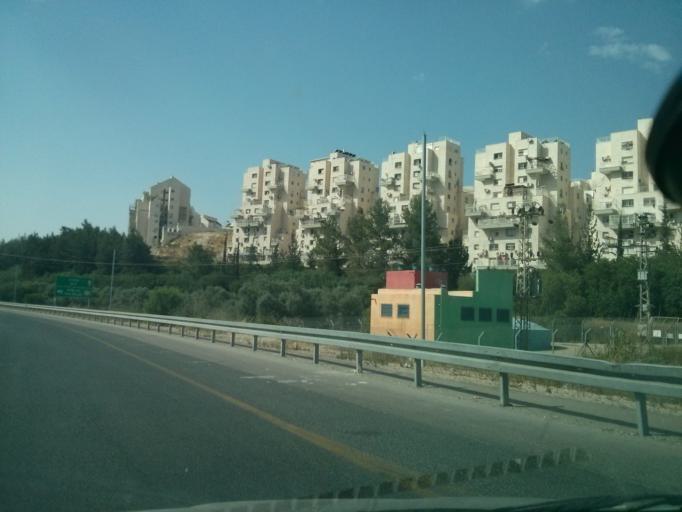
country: IL
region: Jerusalem
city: Bet Shemesh
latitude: 31.7513
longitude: 35.0008
